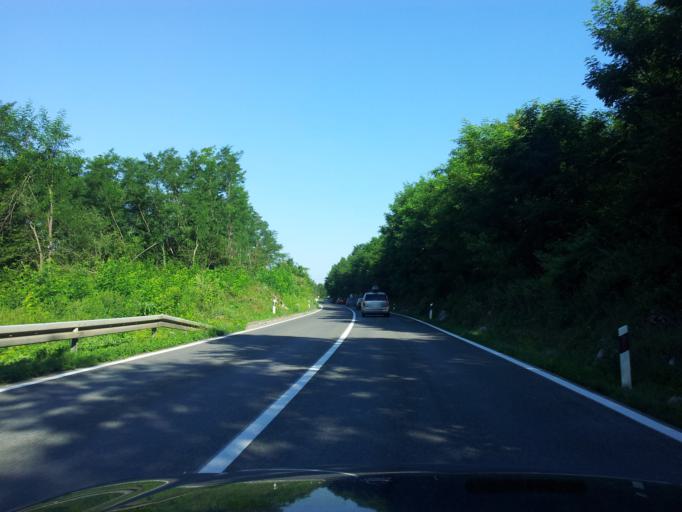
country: HR
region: Karlovacka
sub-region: Grad Karlovac
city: Slunj
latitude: 45.2051
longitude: 15.5493
